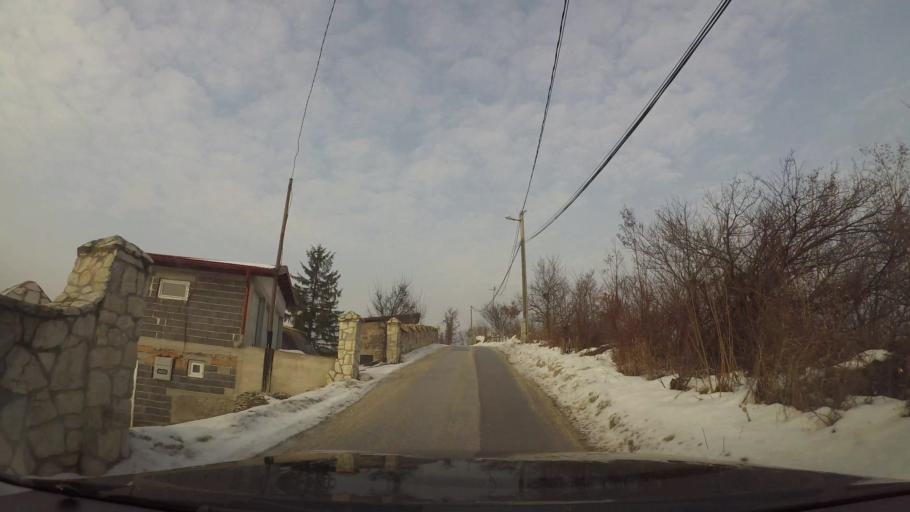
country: BA
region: Federation of Bosnia and Herzegovina
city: Hotonj
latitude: 43.8923
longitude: 18.3819
